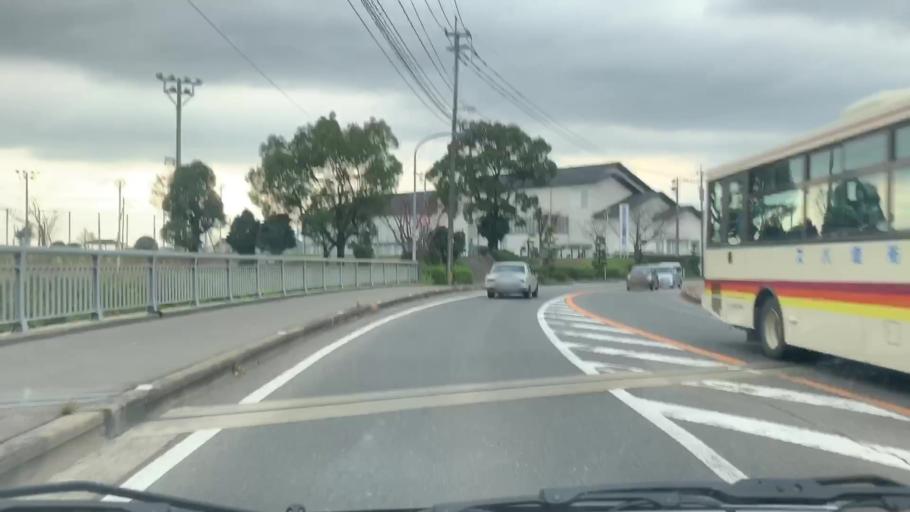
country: JP
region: Saga Prefecture
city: Kashima
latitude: 33.1315
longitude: 130.0615
